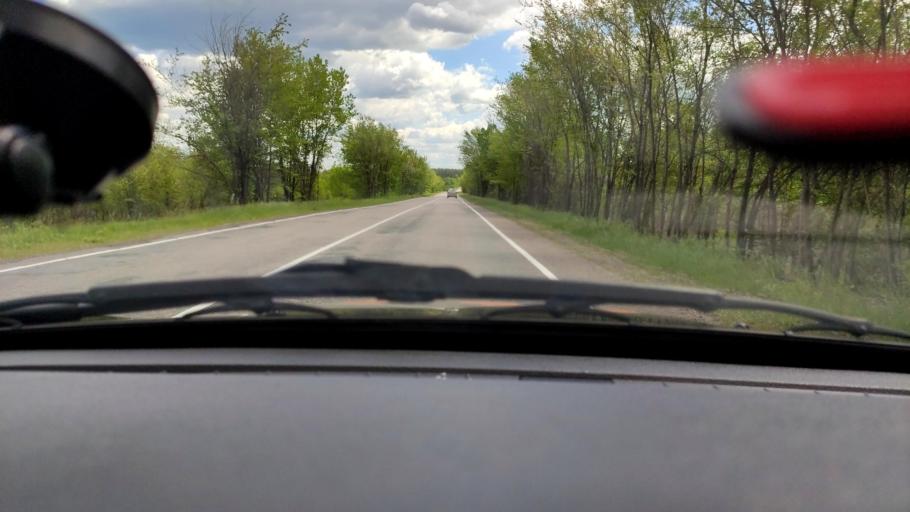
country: RU
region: Belgorod
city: Krasnoye
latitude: 51.0631
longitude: 38.8247
